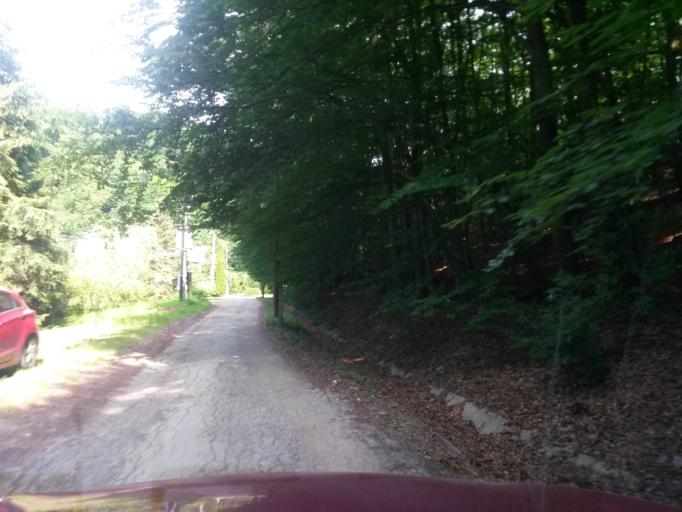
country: SK
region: Kosicky
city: Kosice
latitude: 48.7341
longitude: 21.1225
